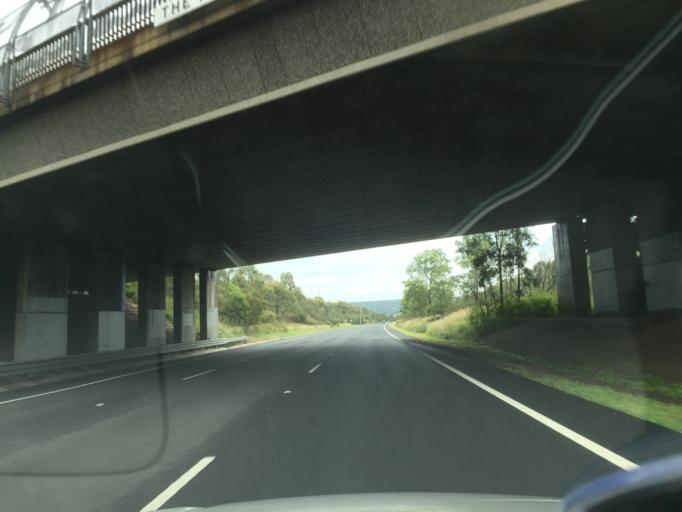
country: AU
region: New South Wales
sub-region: Penrith Municipality
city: Kingswood Park
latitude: -33.7857
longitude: 150.7040
